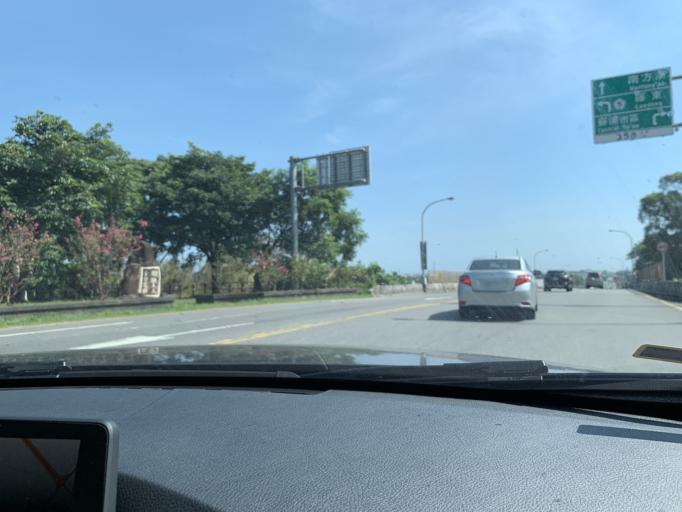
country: TW
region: Taiwan
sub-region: Yilan
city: Yilan
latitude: 24.6139
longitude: 121.8244
